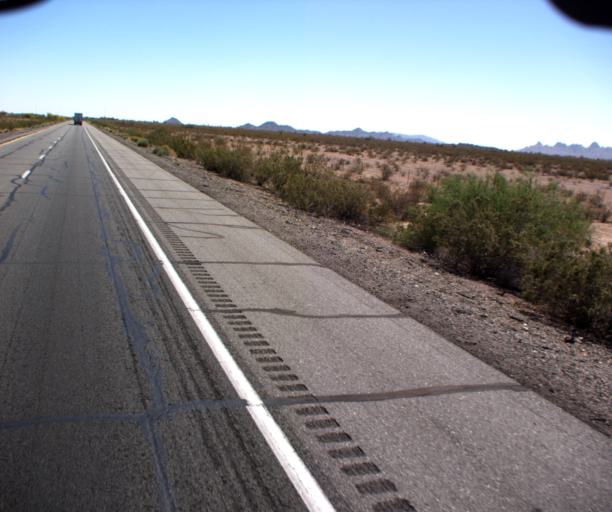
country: US
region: Arizona
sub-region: Maricopa County
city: Buckeye
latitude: 33.5236
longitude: -113.0891
